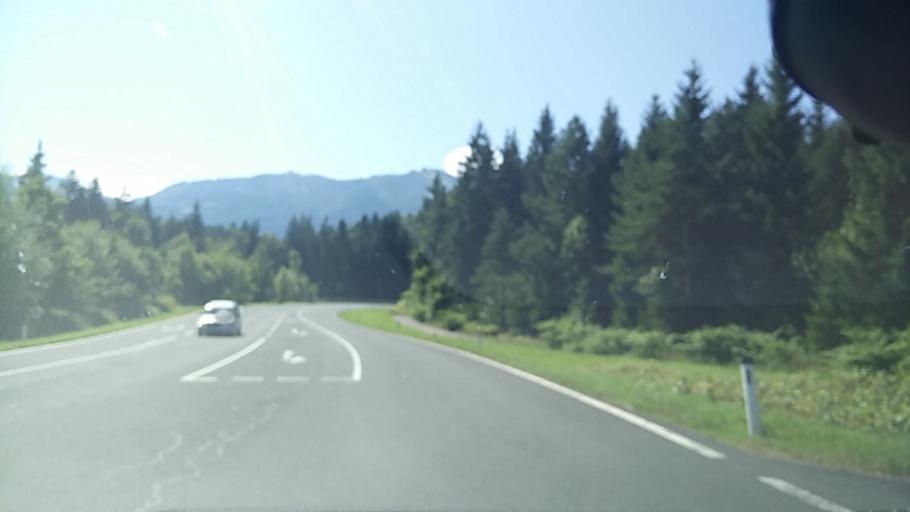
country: AT
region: Carinthia
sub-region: Politischer Bezirk Villach Land
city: Arnoldstein
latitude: 46.5667
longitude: 13.6947
